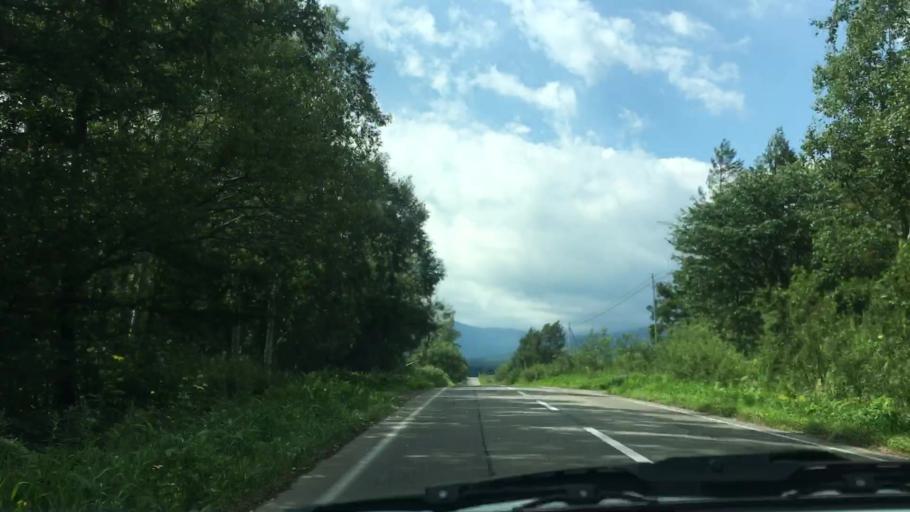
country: JP
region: Hokkaido
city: Otofuke
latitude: 43.2788
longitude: 143.3521
